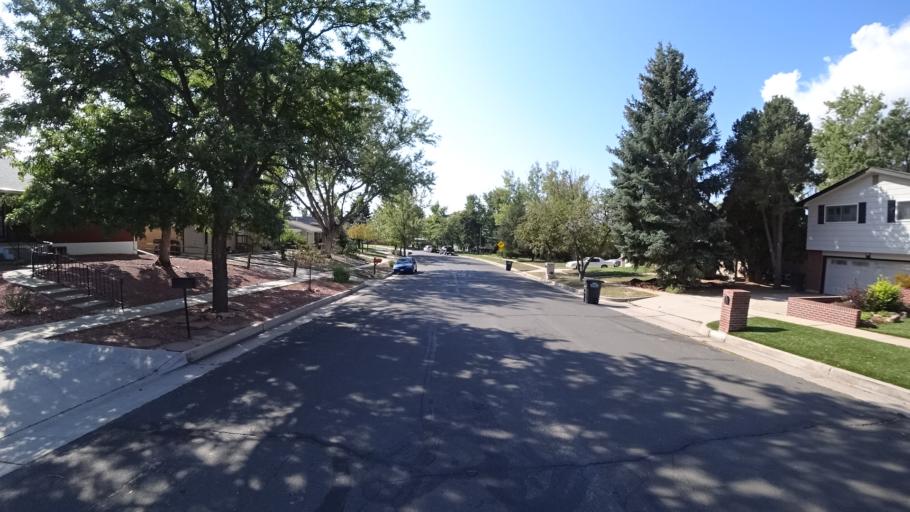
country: US
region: Colorado
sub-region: El Paso County
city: Colorado Springs
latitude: 38.8677
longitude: -104.7756
